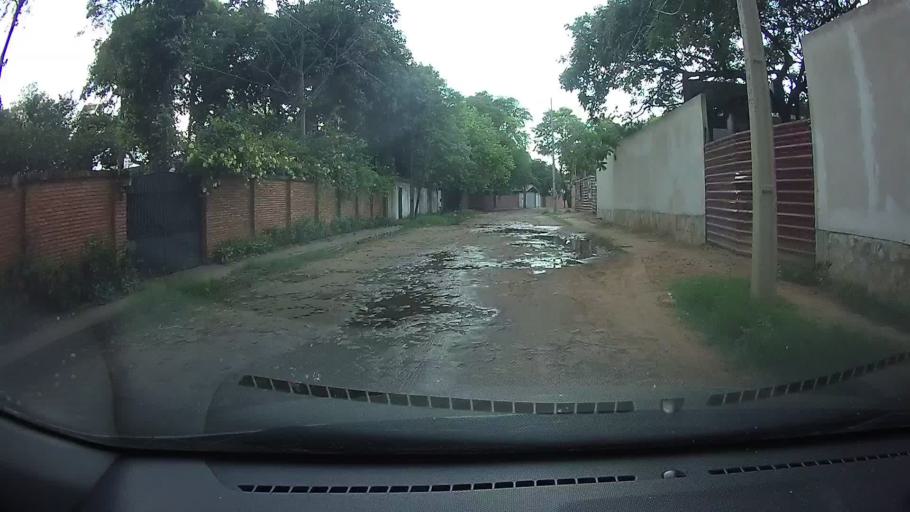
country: PY
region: Asuncion
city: Asuncion
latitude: -25.2651
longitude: -57.5784
